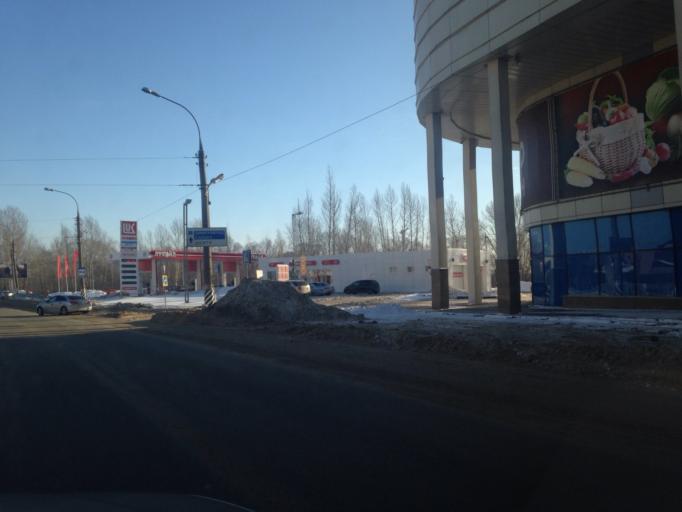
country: RU
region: Ulyanovsk
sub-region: Ulyanovskiy Rayon
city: Ulyanovsk
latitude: 54.3053
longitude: 48.3532
